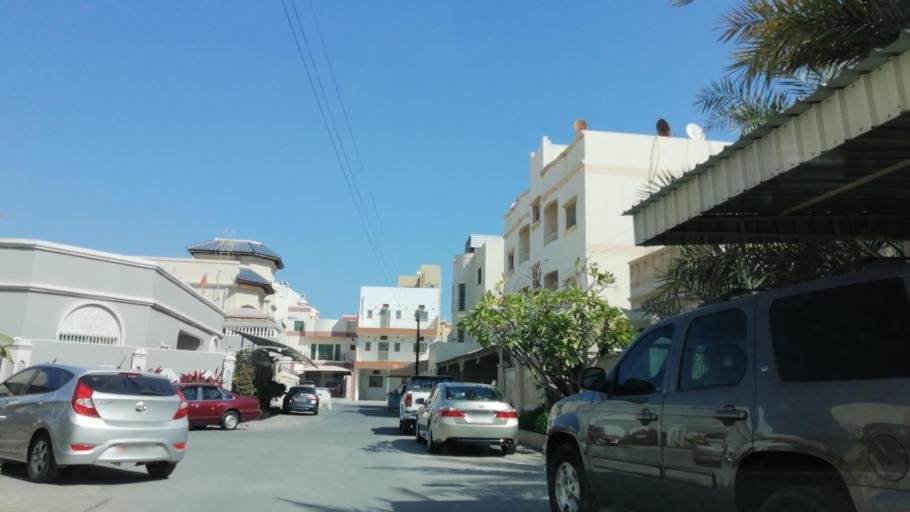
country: BH
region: Muharraq
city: Al Hadd
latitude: 26.2472
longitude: 50.6380
